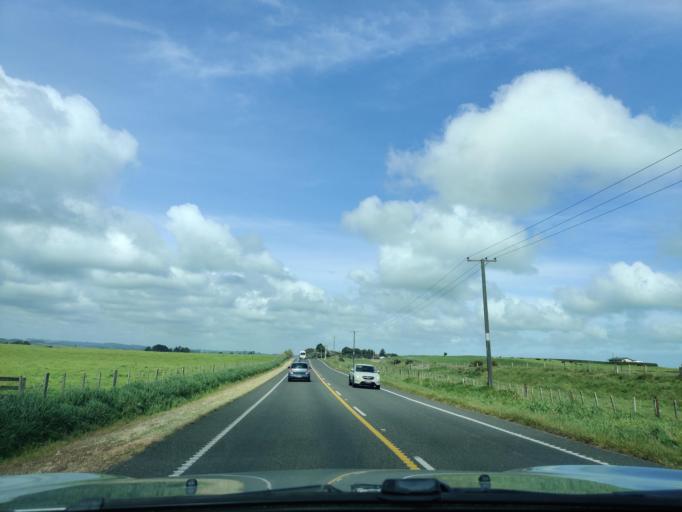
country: NZ
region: Taranaki
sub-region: South Taranaki District
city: Patea
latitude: -39.7750
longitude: 174.6794
